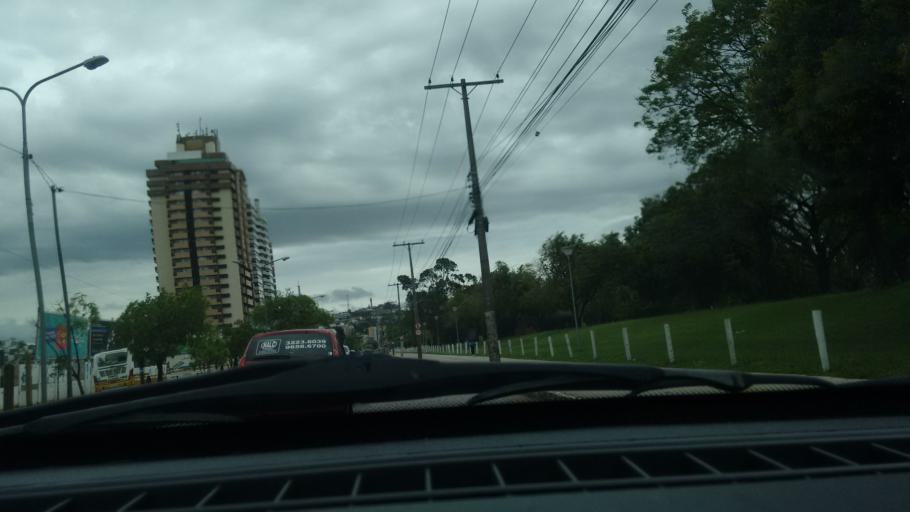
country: BR
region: Rio Grande do Sul
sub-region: Porto Alegre
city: Porto Alegre
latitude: -30.0531
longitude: -51.2301
